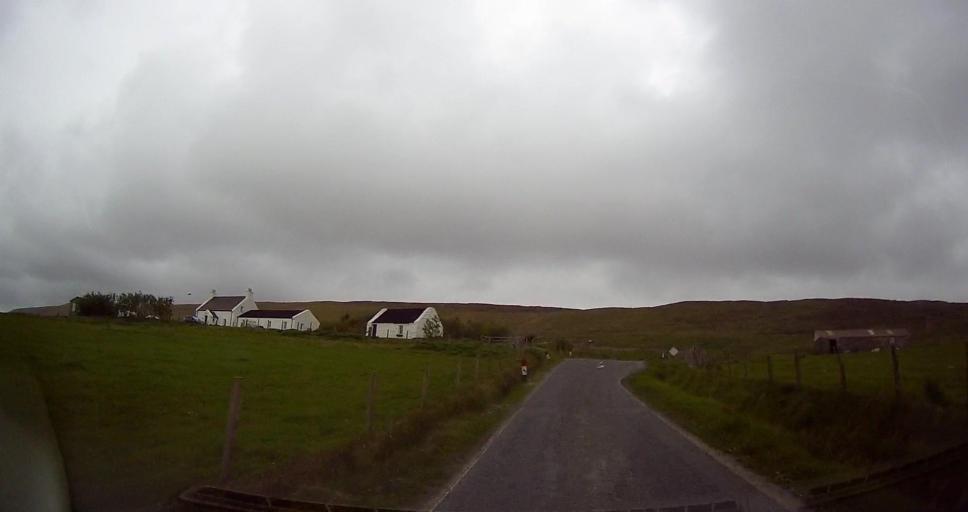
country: GB
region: Scotland
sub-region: Shetland Islands
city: Lerwick
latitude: 60.2749
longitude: -1.2803
